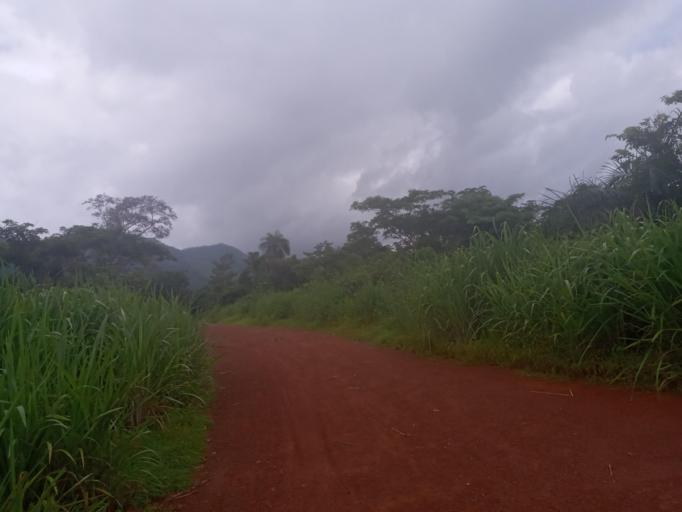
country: SL
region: Northern Province
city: Bumbuna
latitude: 8.9489
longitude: -11.7551
